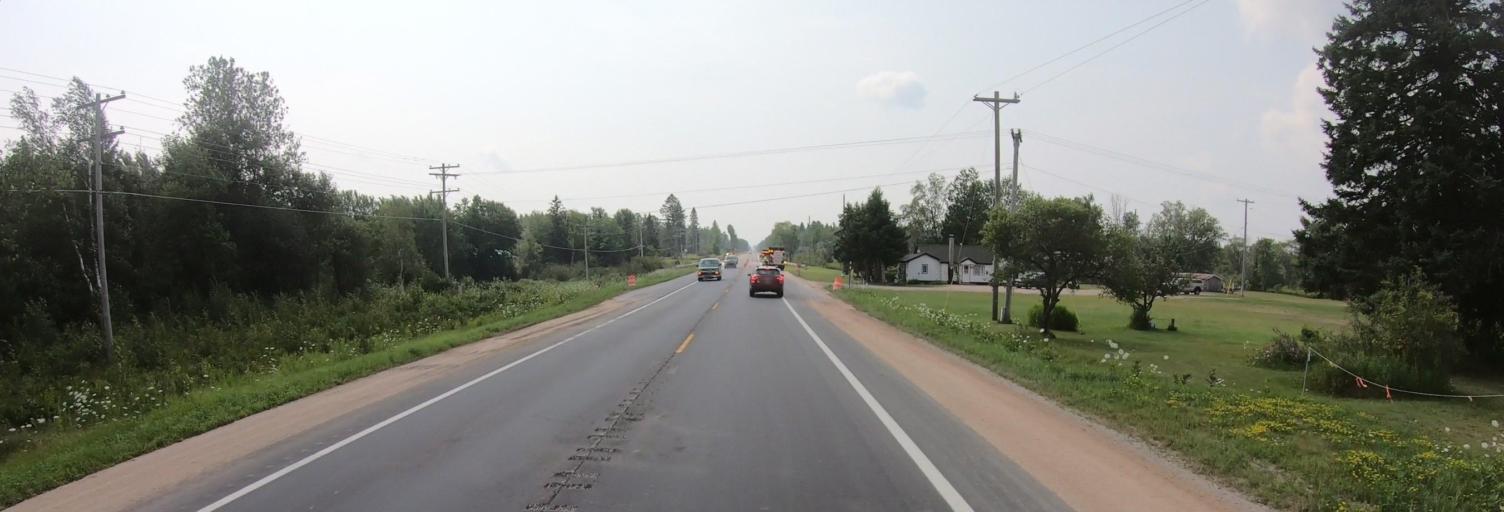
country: US
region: Michigan
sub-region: Luce County
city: Newberry
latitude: 46.3740
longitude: -85.5099
